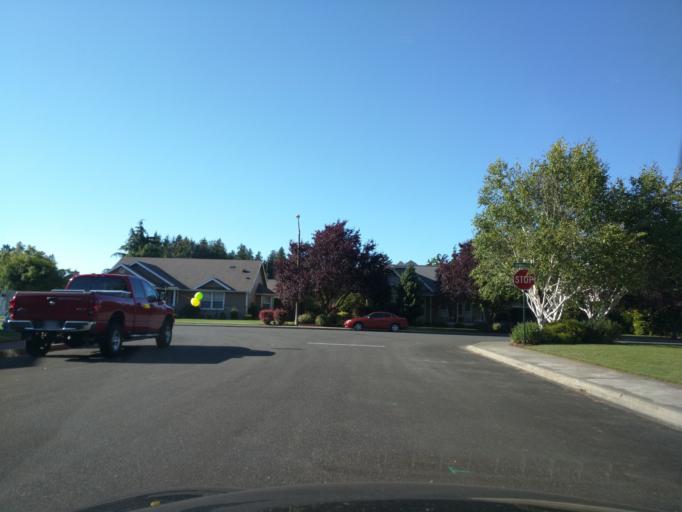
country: US
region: Washington
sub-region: Whatcom County
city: Lynden
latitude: 48.9536
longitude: -122.4482
